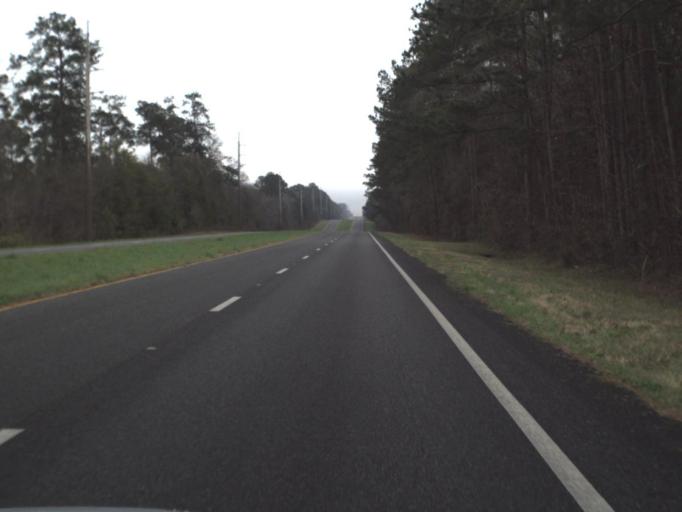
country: US
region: Florida
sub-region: Leon County
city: Woodville
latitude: 30.4023
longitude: -84.0463
